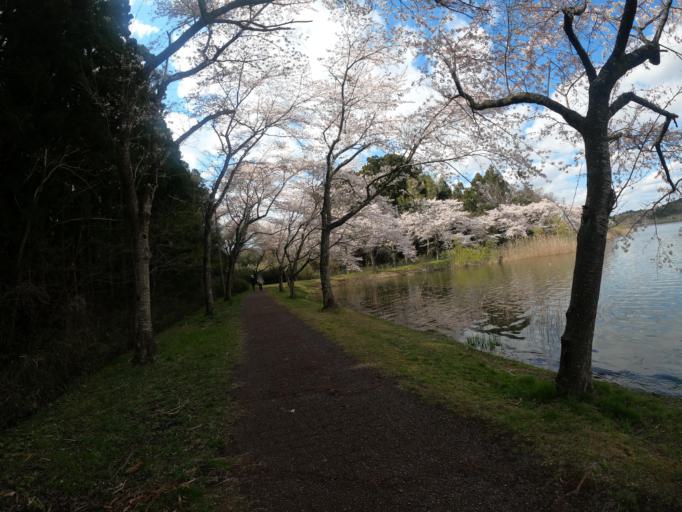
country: JP
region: Miyagi
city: Wakuya
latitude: 38.6146
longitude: 141.2336
